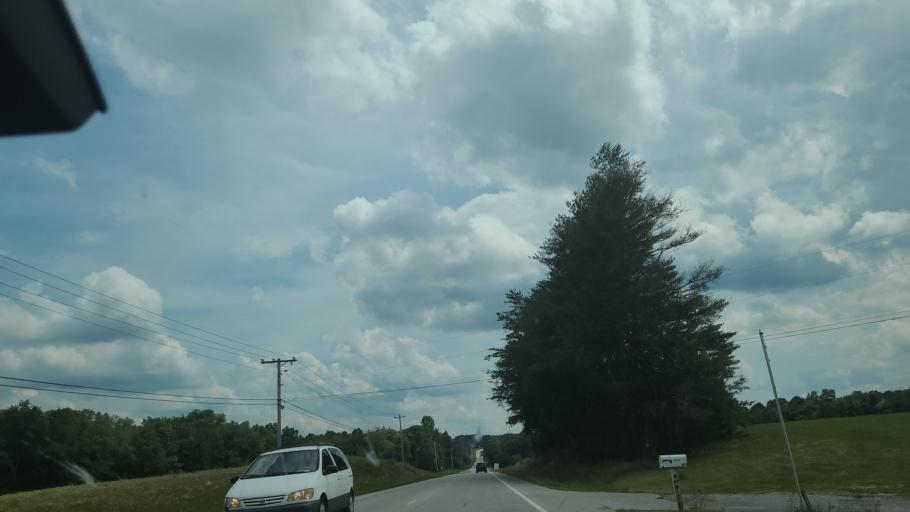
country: US
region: Tennessee
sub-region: Cumberland County
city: Lake Tansi
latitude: 35.8149
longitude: -85.0199
